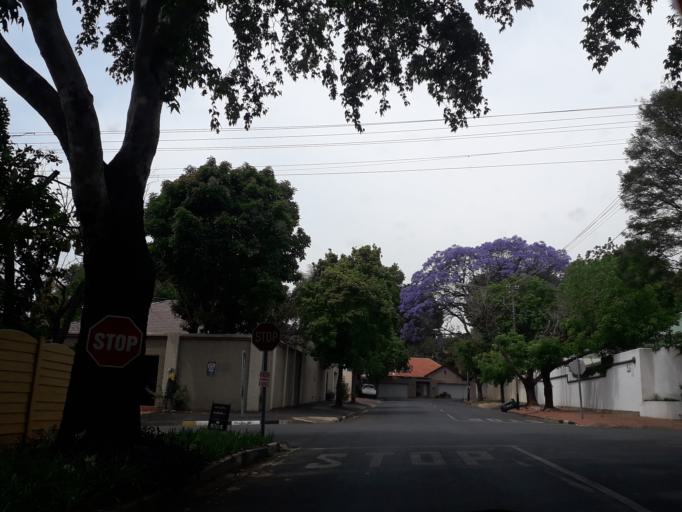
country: ZA
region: Gauteng
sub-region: City of Johannesburg Metropolitan Municipality
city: Johannesburg
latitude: -26.1580
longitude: 28.0783
